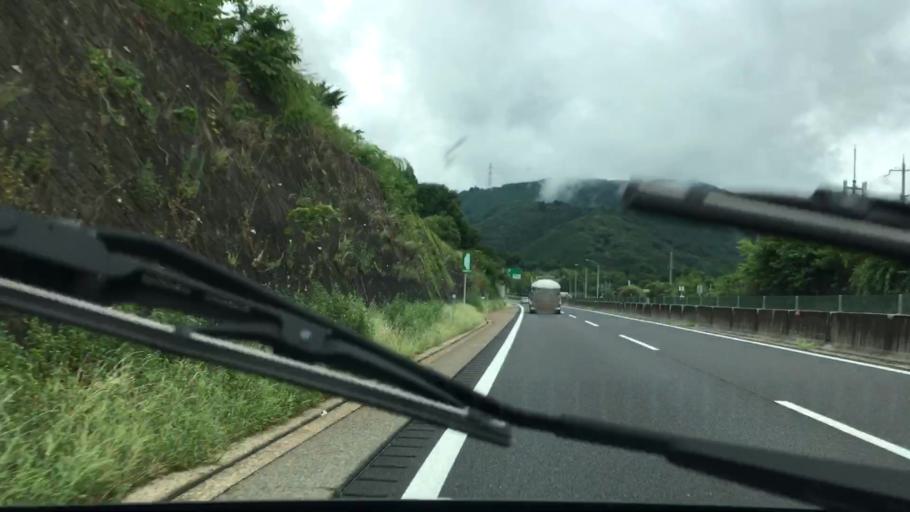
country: JP
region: Hyogo
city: Yamazakicho-nakabirose
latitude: 35.0276
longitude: 134.4898
